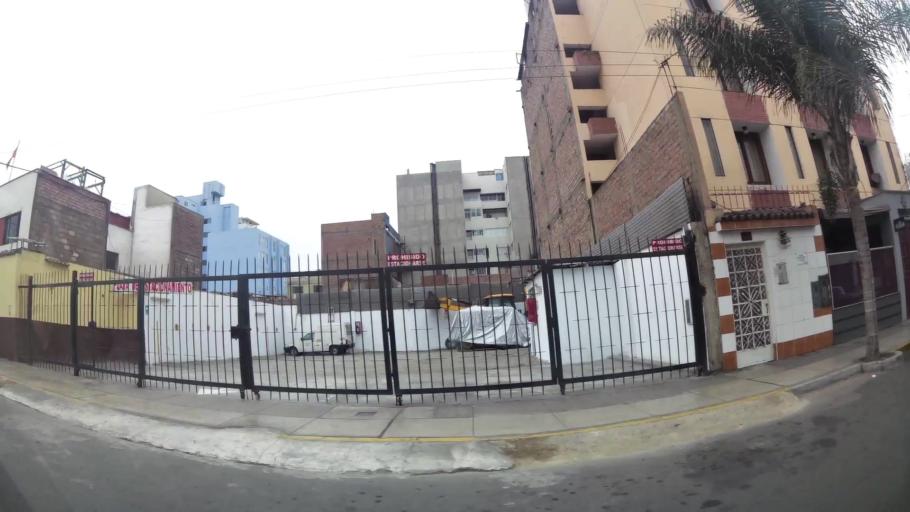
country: PE
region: Lima
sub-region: Lima
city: San Isidro
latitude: -12.1166
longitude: -77.0358
